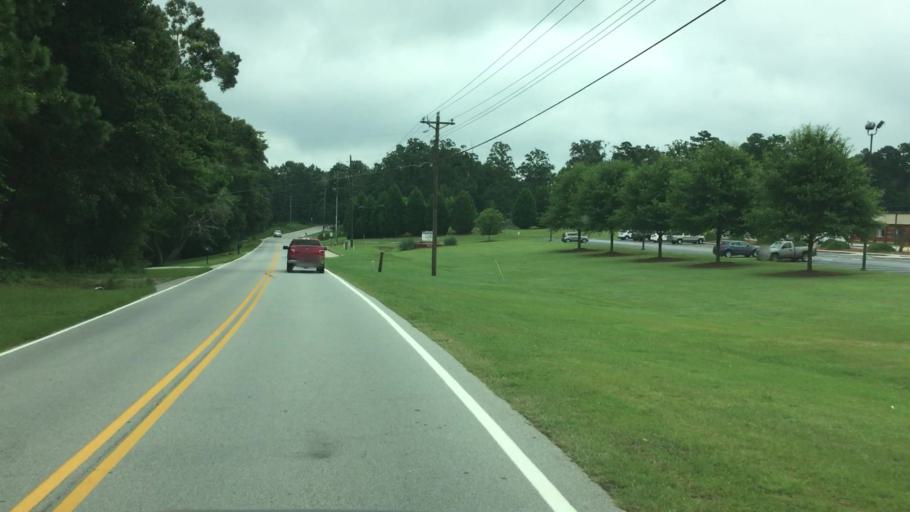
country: US
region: Georgia
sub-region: Barrow County
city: Winder
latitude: 34.0268
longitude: -83.7400
